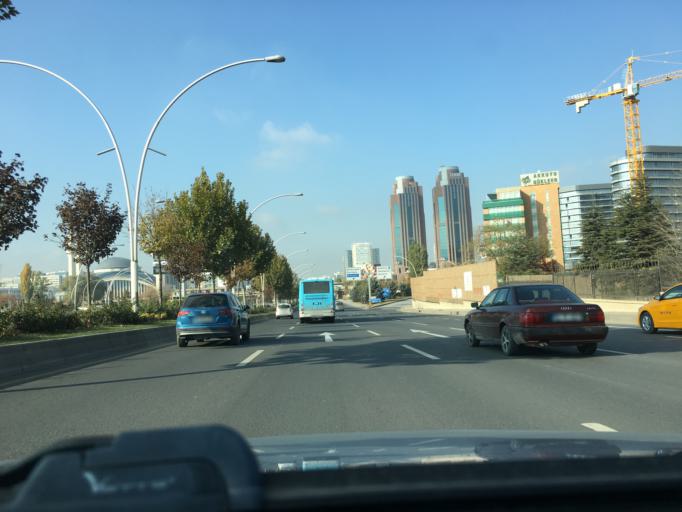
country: TR
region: Ankara
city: Batikent
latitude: 39.9080
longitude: 32.7684
